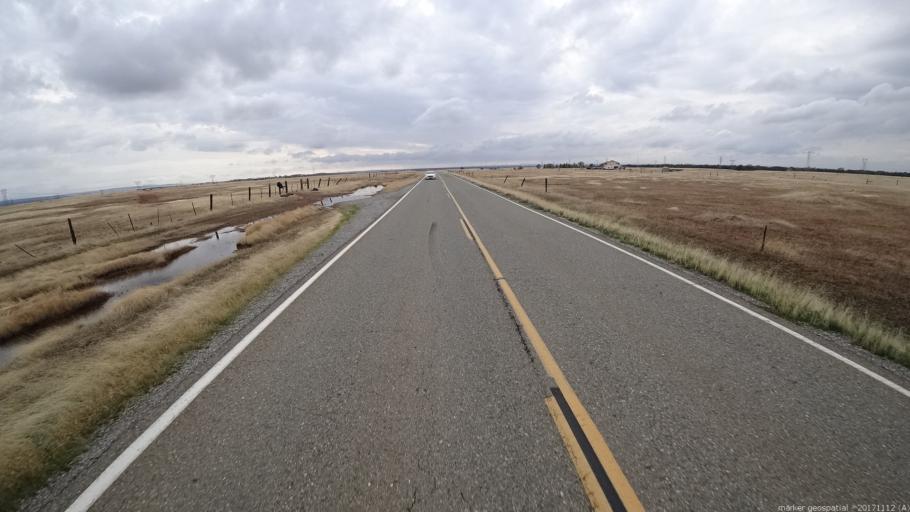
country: US
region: California
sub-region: Shasta County
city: Palo Cedro
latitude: 40.5192
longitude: -122.1805
